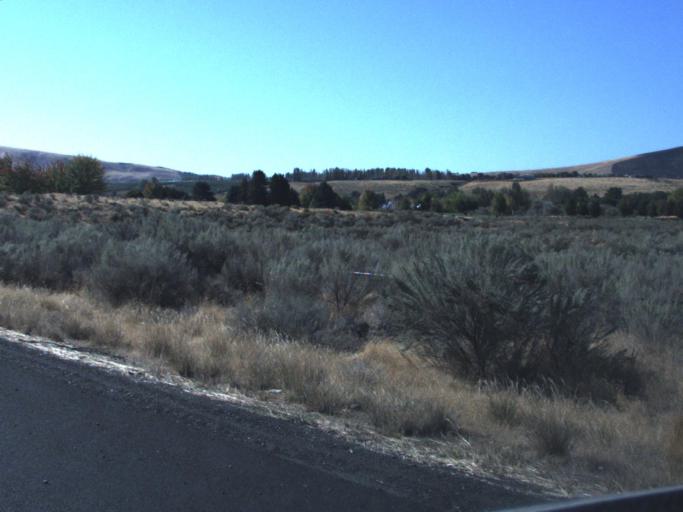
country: US
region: Washington
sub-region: Benton County
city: Richland
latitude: 46.2850
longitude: -119.3067
